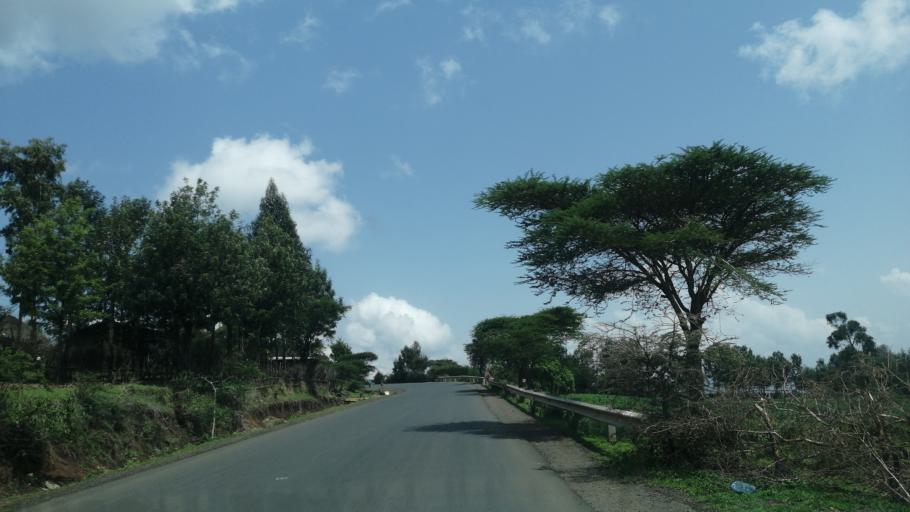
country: ET
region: Oromiya
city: Guder
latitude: 8.9941
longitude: 37.6231
